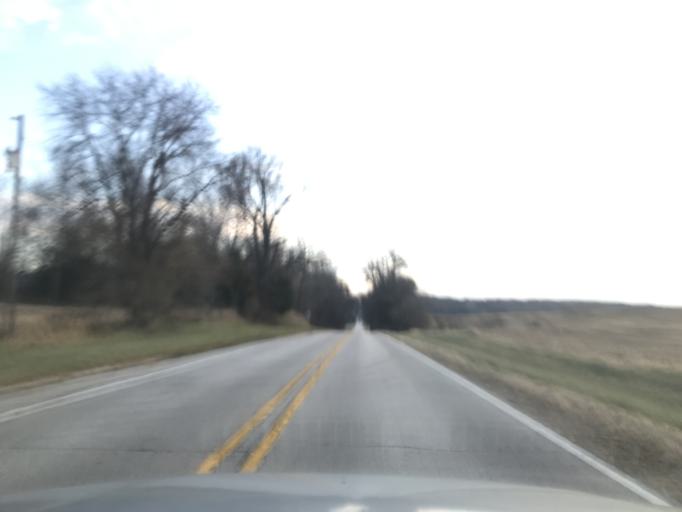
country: US
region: Illinois
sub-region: Henderson County
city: Oquawka
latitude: 41.0104
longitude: -90.8534
